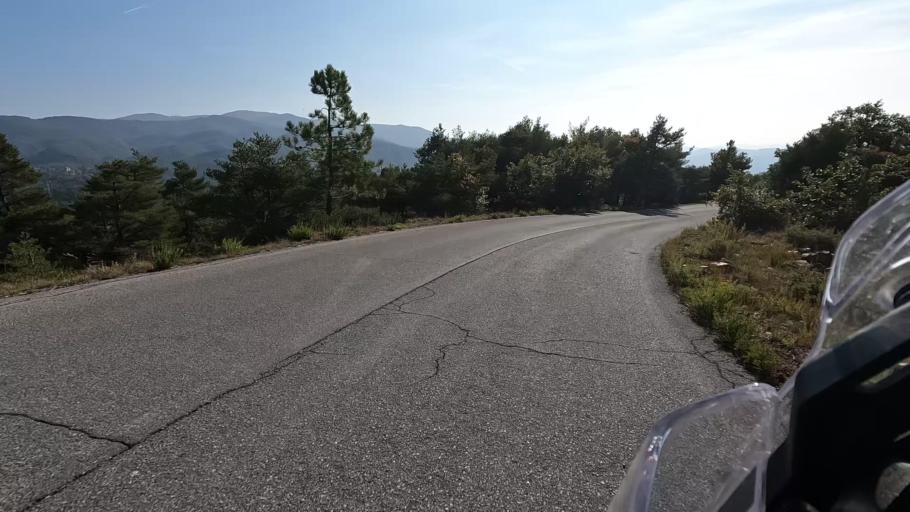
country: IT
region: Liguria
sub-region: Provincia di Savona
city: Sassello
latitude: 44.5067
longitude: 8.5368
